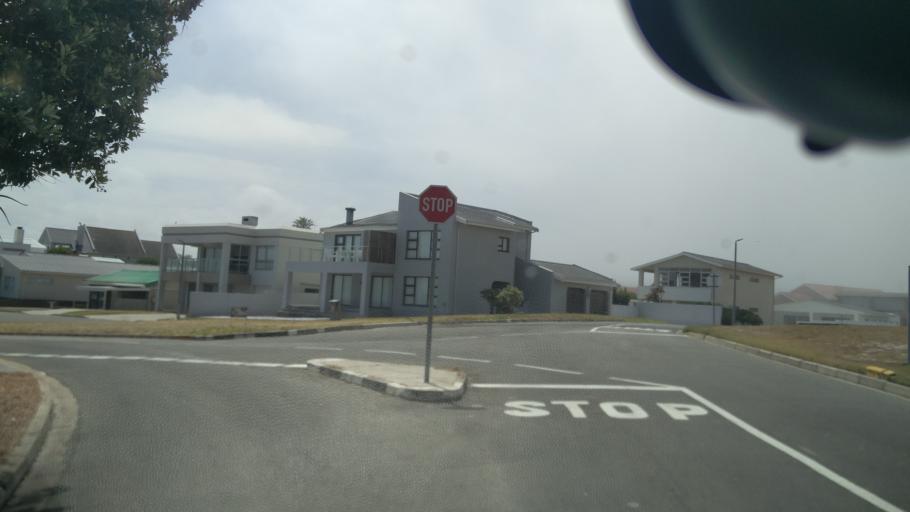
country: ZA
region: Western Cape
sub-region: City of Cape Town
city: Atlantis
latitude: -33.3485
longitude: 18.1534
